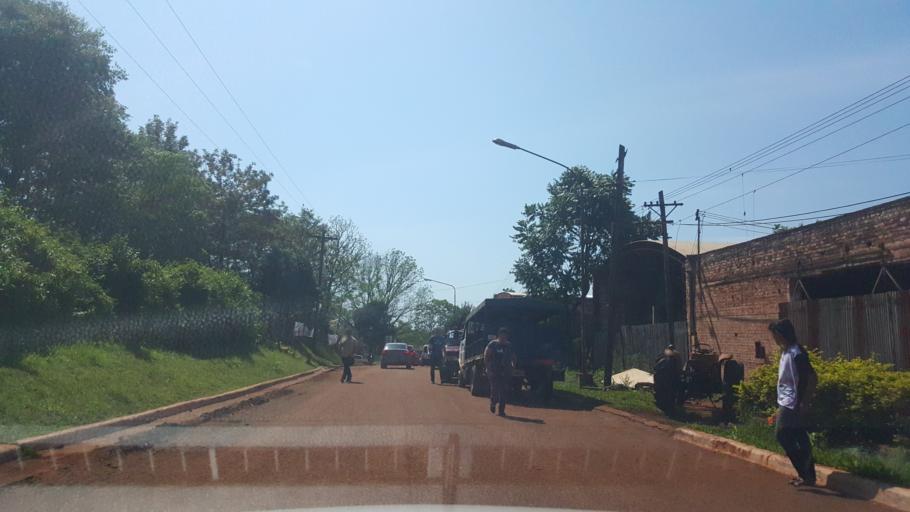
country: AR
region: Corrientes
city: San Carlos
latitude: -27.7450
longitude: -55.8964
